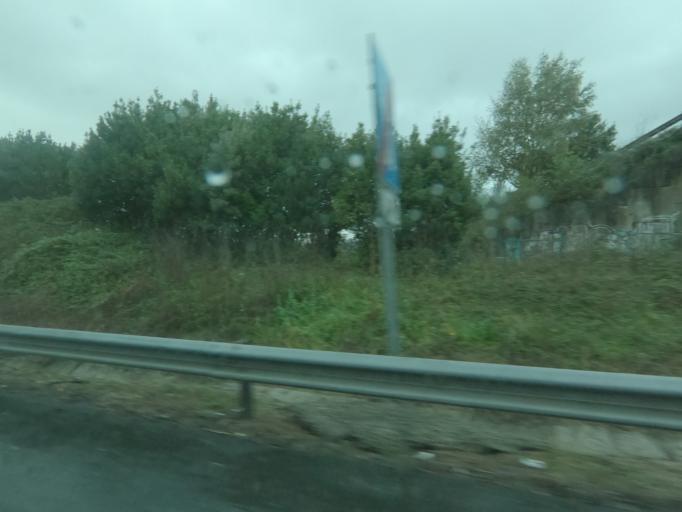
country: ES
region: Galicia
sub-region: Provincia de Pontevedra
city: Pontevedra
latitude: 42.4377
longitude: -8.6501
